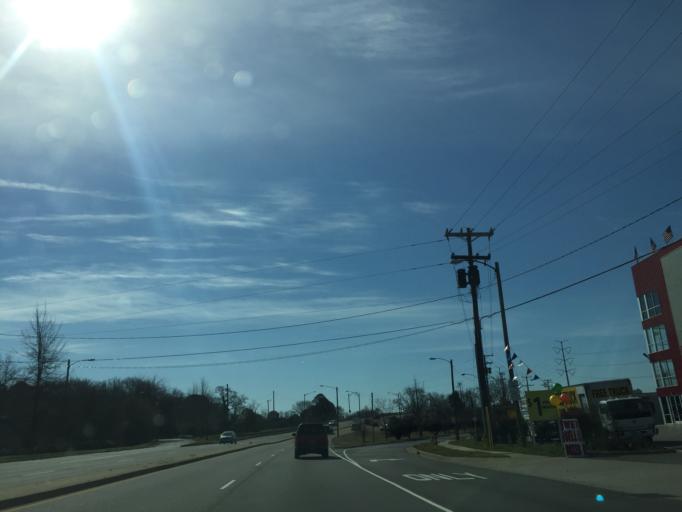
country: US
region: Virginia
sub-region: City of Norfolk
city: Norfolk
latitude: 36.9002
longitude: -76.2561
